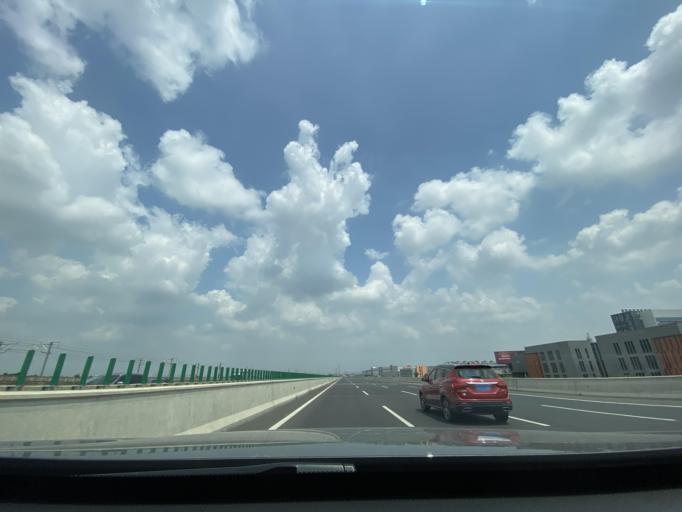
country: CN
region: Sichuan
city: Longquan
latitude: 30.5225
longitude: 104.1725
